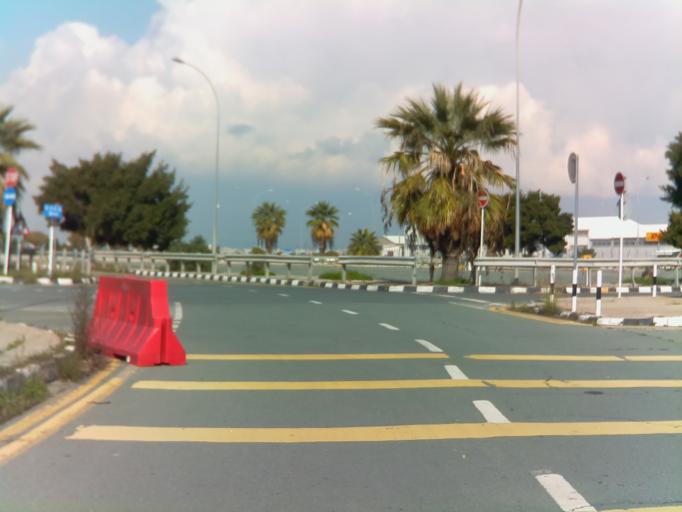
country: CY
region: Larnaka
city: Meneou
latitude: 34.8815
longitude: 33.6246
